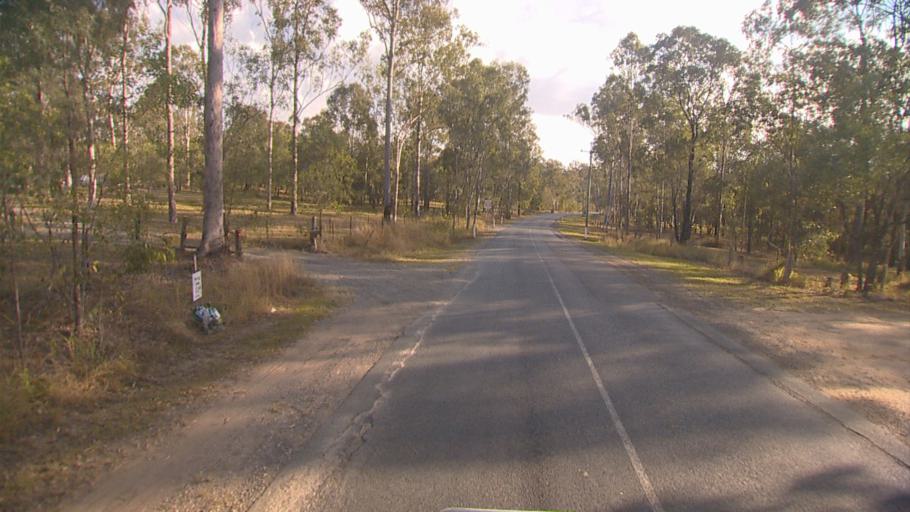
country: AU
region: Queensland
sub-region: Logan
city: Cedar Vale
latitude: -27.8479
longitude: 153.1015
